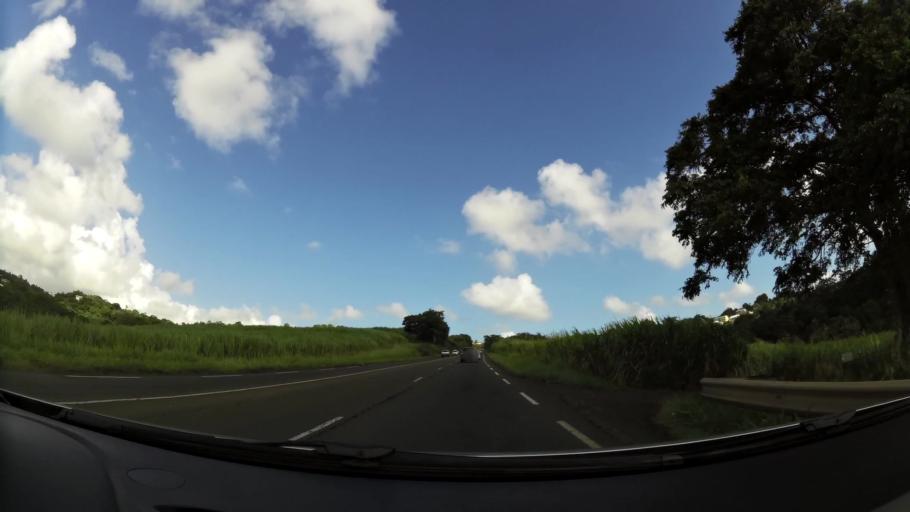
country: MQ
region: Martinique
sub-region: Martinique
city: Le Robert
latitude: 14.6926
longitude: -60.9408
